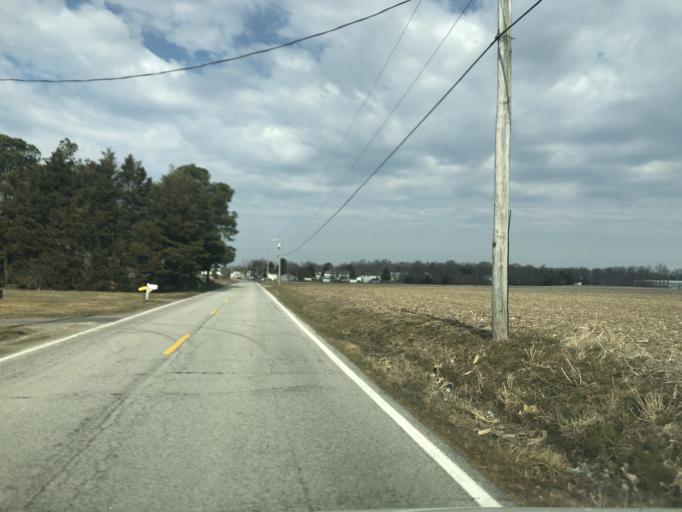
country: US
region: Maryland
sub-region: Queen Anne's County
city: Centreville
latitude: 39.0936
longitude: -75.9529
